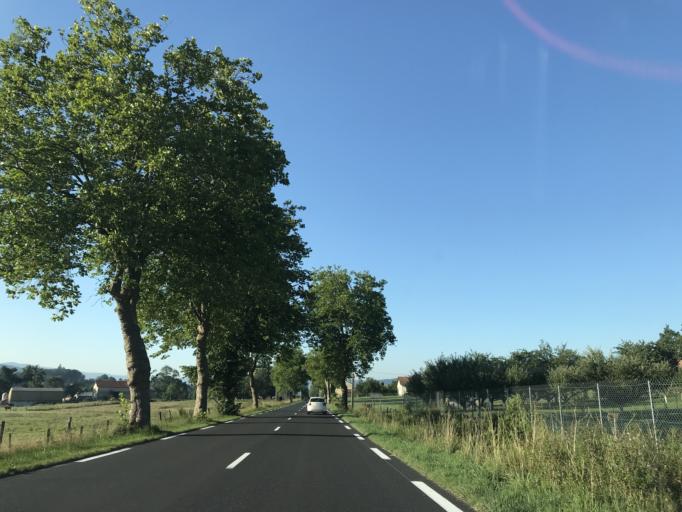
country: FR
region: Auvergne
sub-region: Departement du Puy-de-Dome
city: Ambert
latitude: 45.5669
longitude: 3.7445
